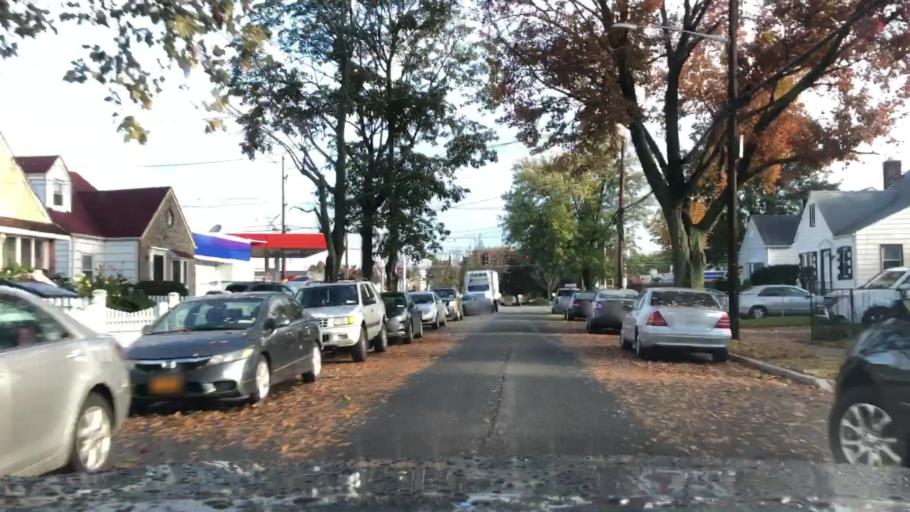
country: US
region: New York
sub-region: Nassau County
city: South Floral Park
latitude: 40.7066
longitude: -73.7025
